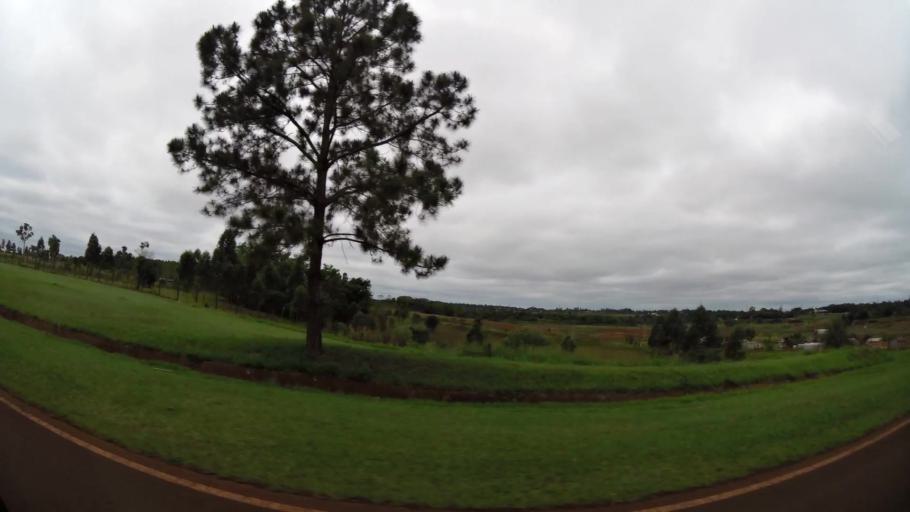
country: PY
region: Alto Parana
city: Colonia Yguazu
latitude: -25.4782
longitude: -54.8609
